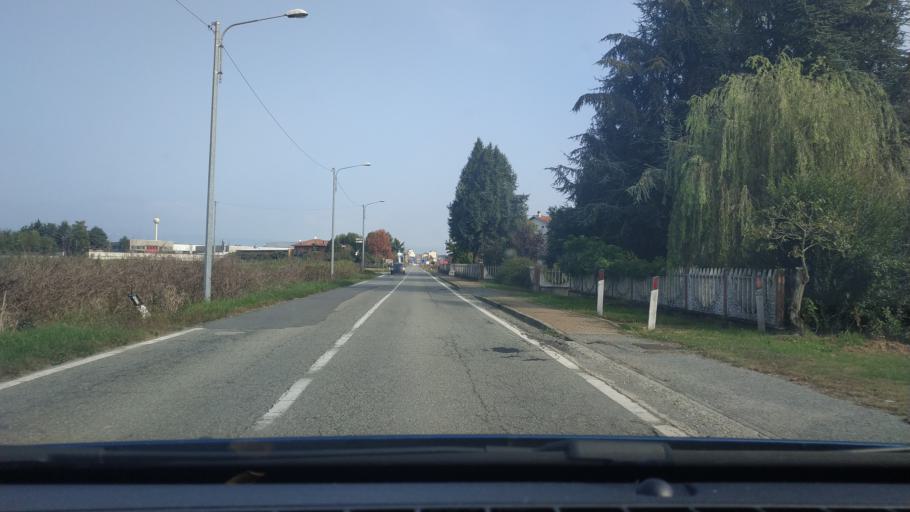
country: IT
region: Piedmont
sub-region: Provincia di Torino
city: Scarmagno
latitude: 45.3709
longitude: 7.8499
